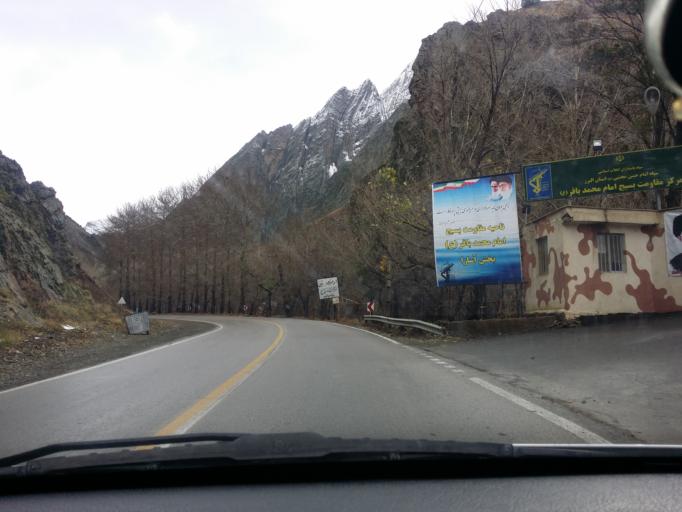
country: IR
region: Tehran
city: Tajrish
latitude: 36.0219
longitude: 51.2644
